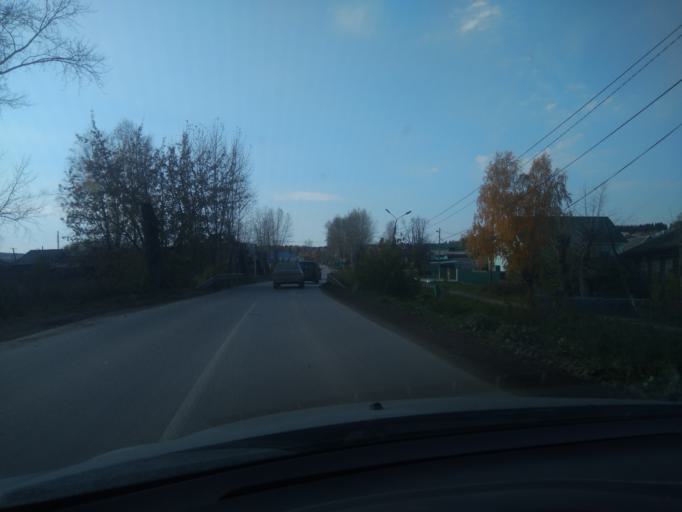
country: RU
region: Sverdlovsk
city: Nizhniye Sergi
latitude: 56.6583
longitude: 59.3008
